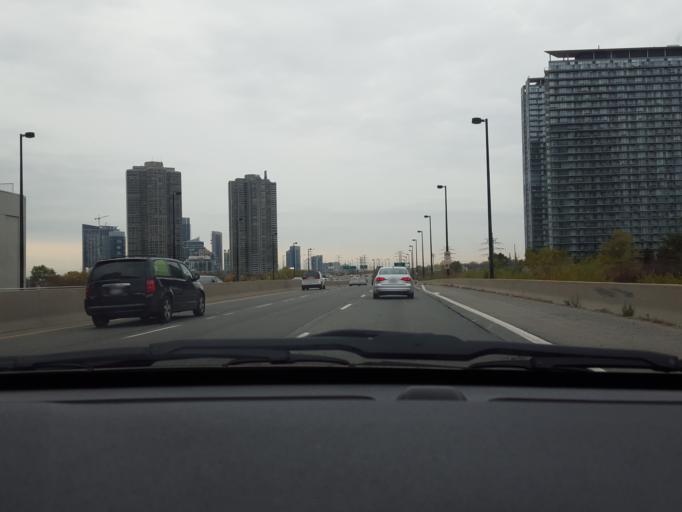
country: CA
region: Ontario
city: Toronto
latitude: 43.6368
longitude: -79.4665
